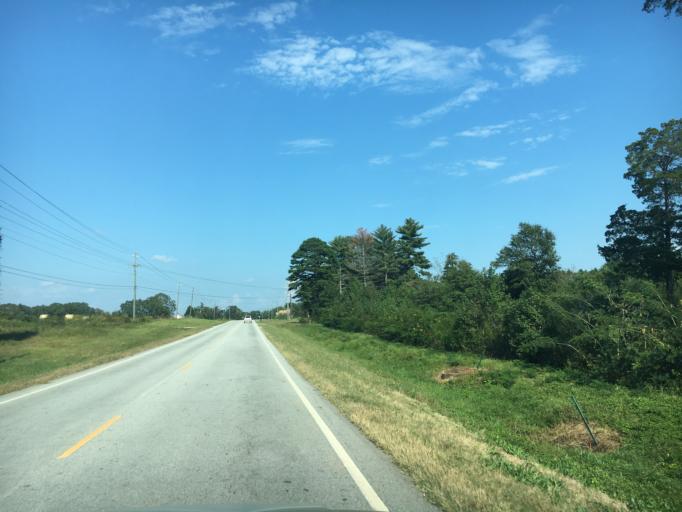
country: US
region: Georgia
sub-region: Franklin County
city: Lavonia
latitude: 34.4577
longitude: -83.0879
